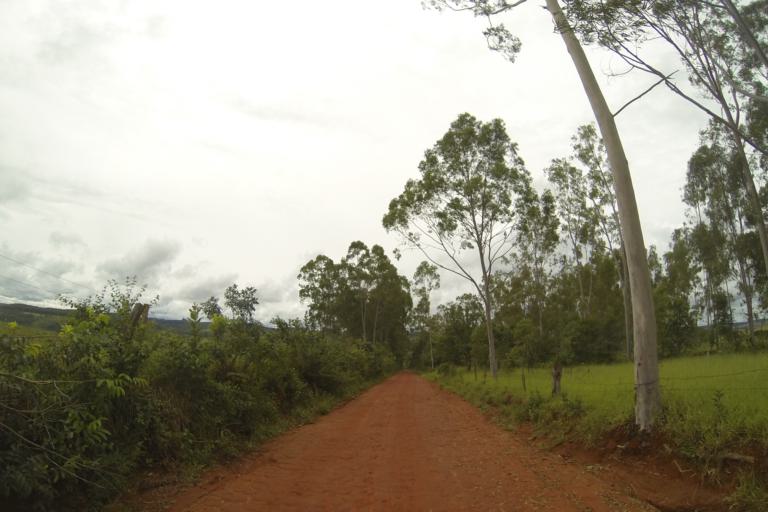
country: BR
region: Minas Gerais
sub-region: Ibia
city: Ibia
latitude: -19.6805
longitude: -46.6805
